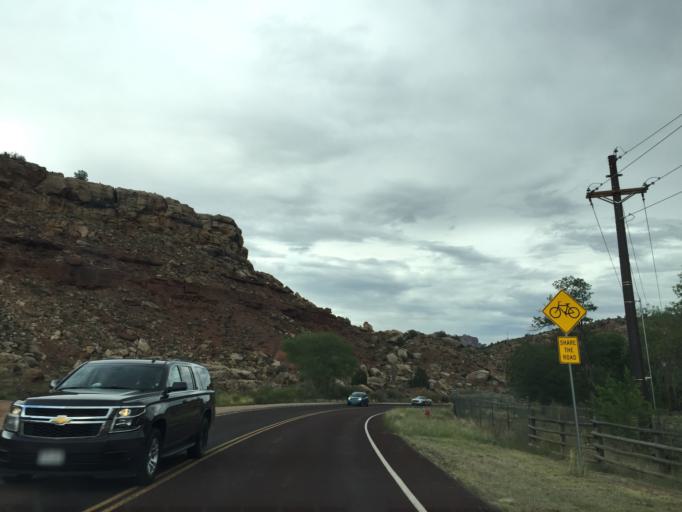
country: US
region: Utah
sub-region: Washington County
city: Hildale
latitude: 37.1610
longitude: -113.0325
